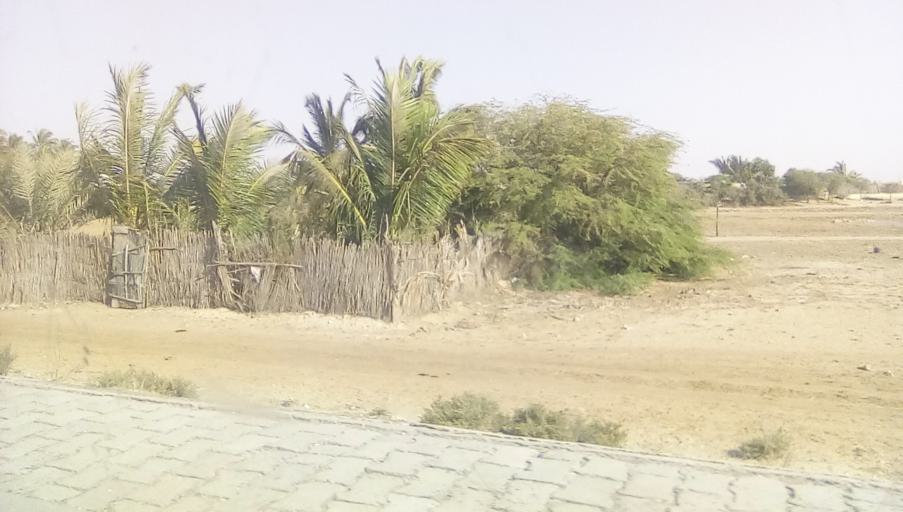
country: SN
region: Saint-Louis
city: Saint-Louis
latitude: 16.0376
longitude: -16.4631
